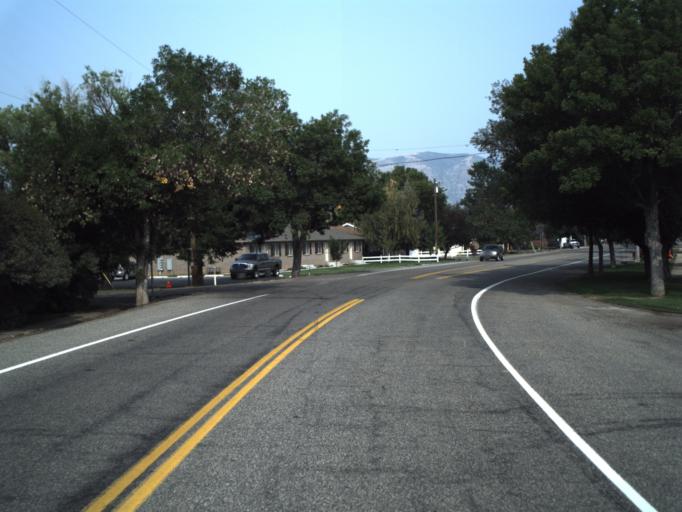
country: US
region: Utah
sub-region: Summit County
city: Coalville
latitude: 41.0146
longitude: -111.4964
